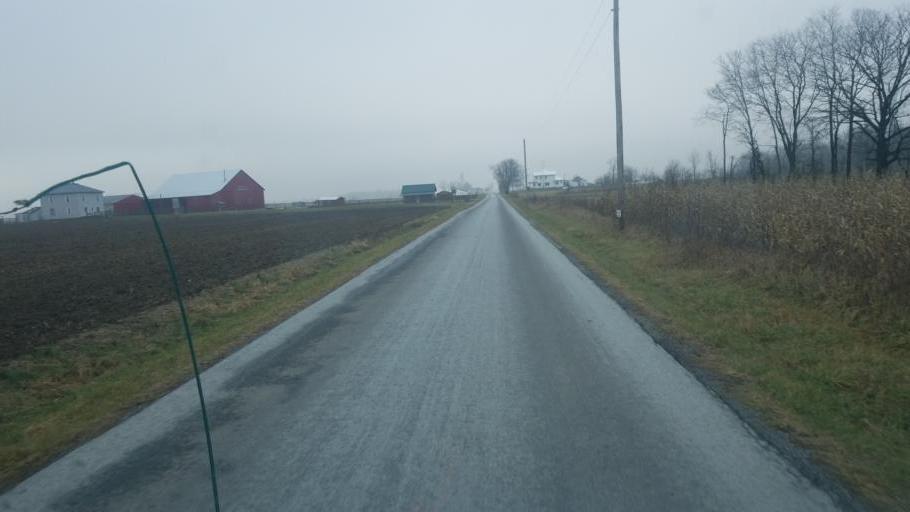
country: US
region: Ohio
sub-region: Hardin County
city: Kenton
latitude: 40.6460
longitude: -83.4771
